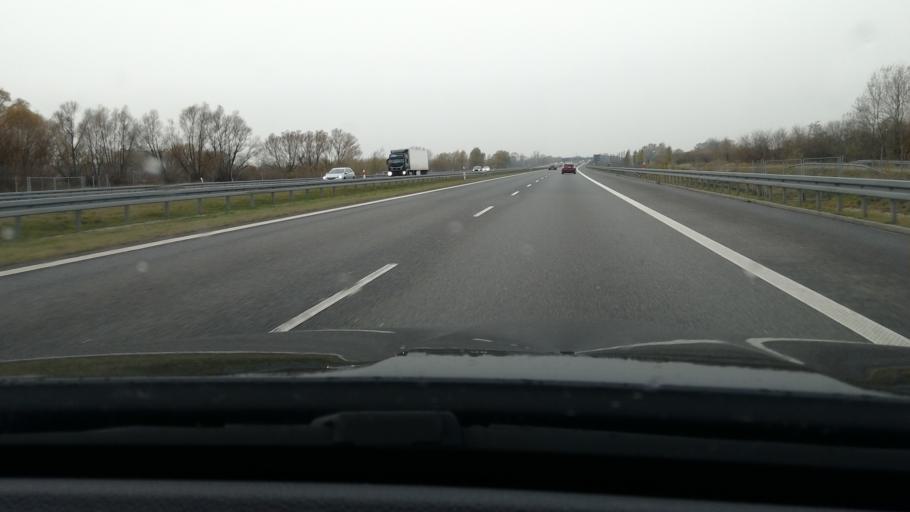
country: PL
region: Masovian Voivodeship
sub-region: Powiat warszawski zachodni
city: Bieniewice
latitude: 52.1226
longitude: 20.5214
